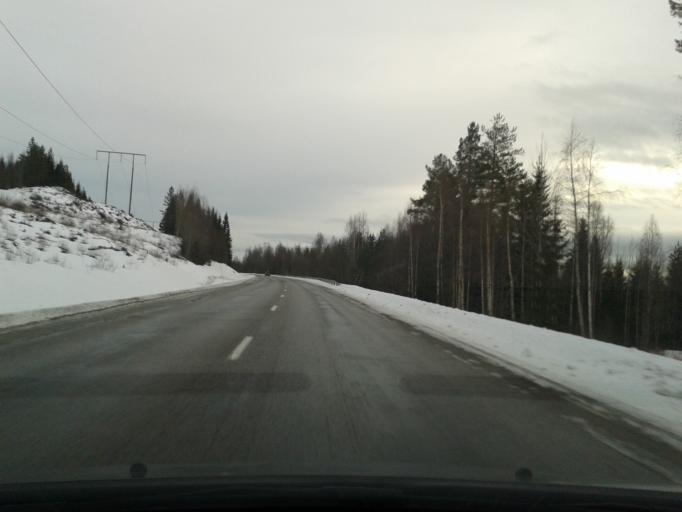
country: SE
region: Vaesternorrland
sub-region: Solleftea Kommun
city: As
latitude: 63.5327
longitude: 16.8332
